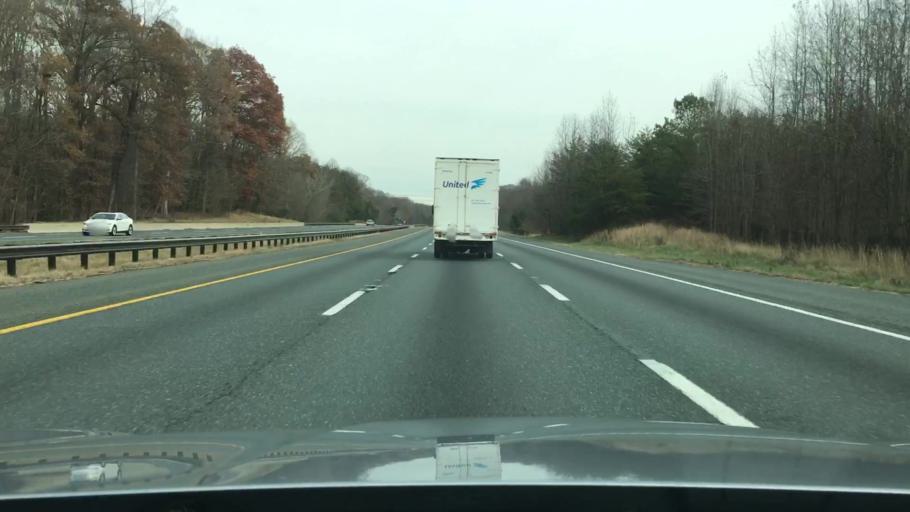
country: US
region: Maryland
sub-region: Anne Arundel County
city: Davidsonville
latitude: 38.9699
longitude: -76.6247
